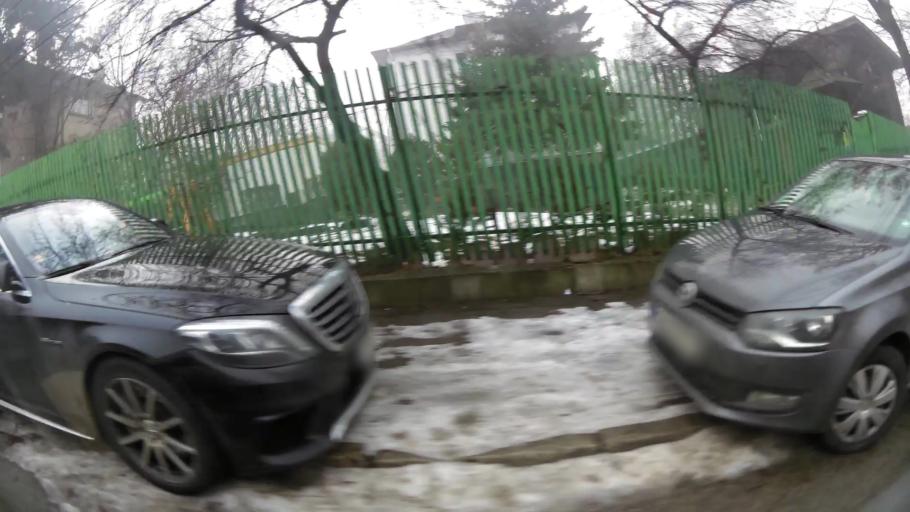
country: BG
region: Sofia-Capital
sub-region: Stolichna Obshtina
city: Sofia
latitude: 42.6594
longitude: 23.2509
